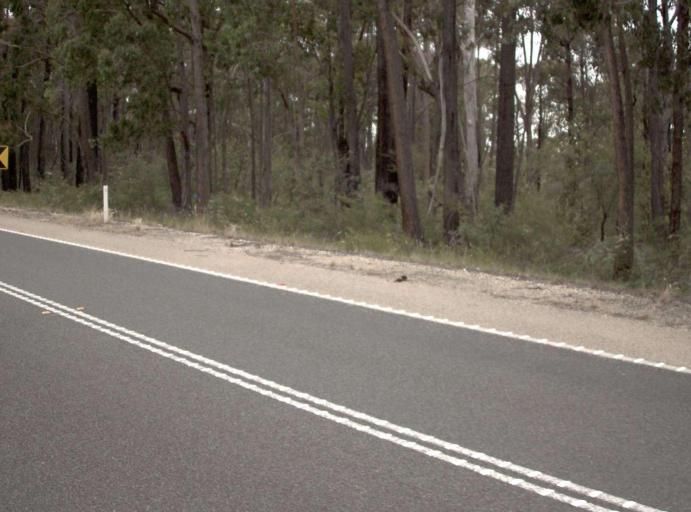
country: AU
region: Victoria
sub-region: East Gippsland
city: Lakes Entrance
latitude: -37.6908
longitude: 148.0231
